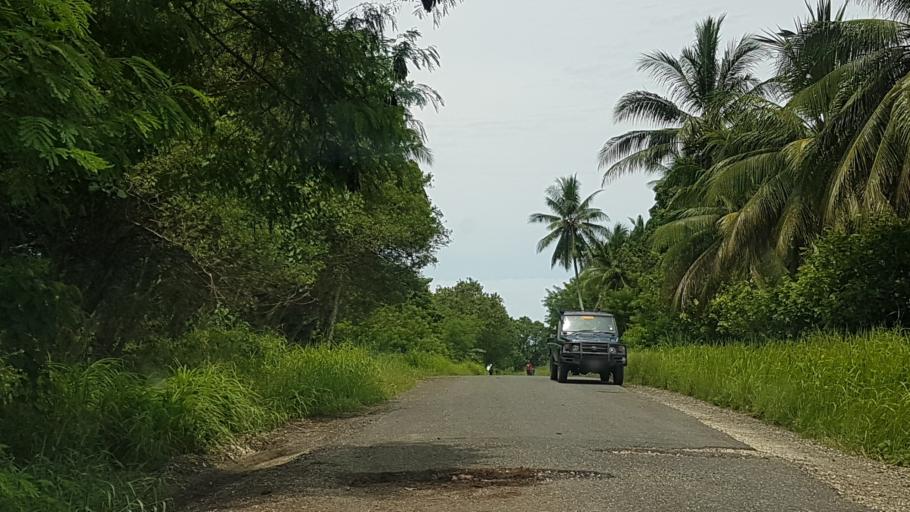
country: PG
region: Madang
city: Madang
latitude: -4.5931
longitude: 145.5411
